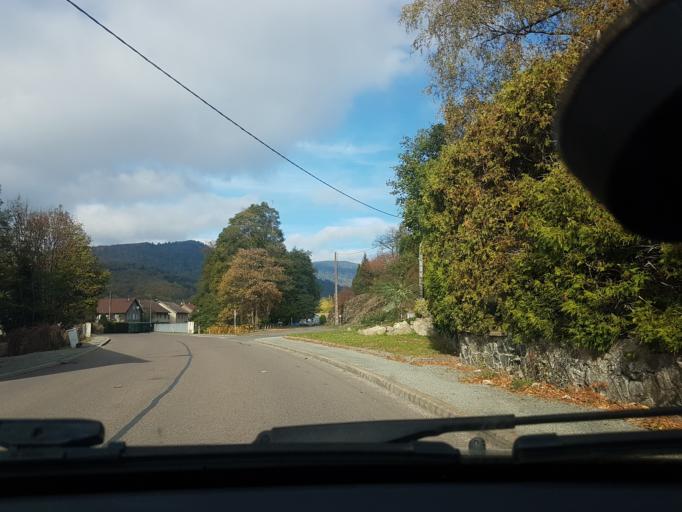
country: FR
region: Franche-Comte
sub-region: Departement de la Haute-Saone
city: Plancher-Bas
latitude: 47.7428
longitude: 6.7289
